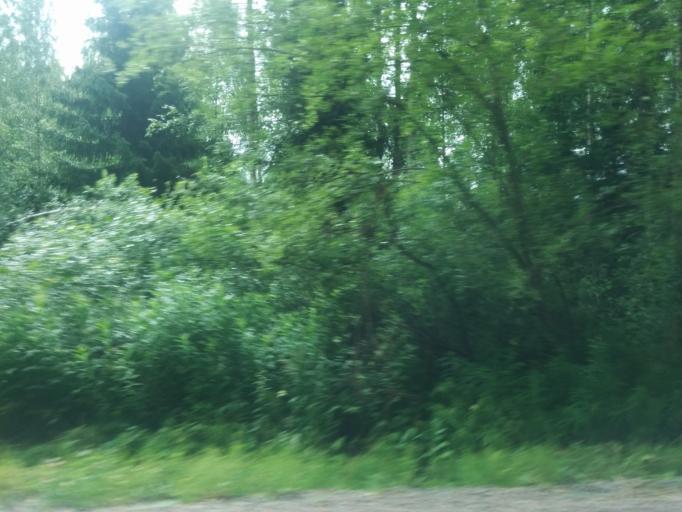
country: FI
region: Pirkanmaa
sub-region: Tampere
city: Kuhmalahti
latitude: 61.6916
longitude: 24.5724
